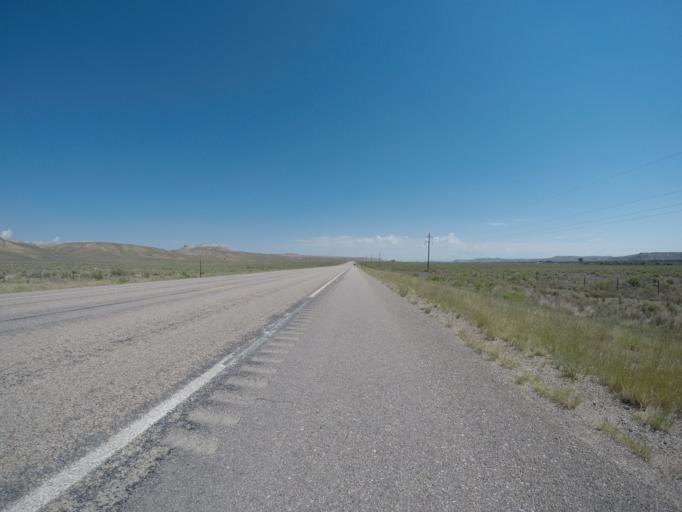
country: US
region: Wyoming
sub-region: Sublette County
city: Marbleton
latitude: 42.3561
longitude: -110.1569
